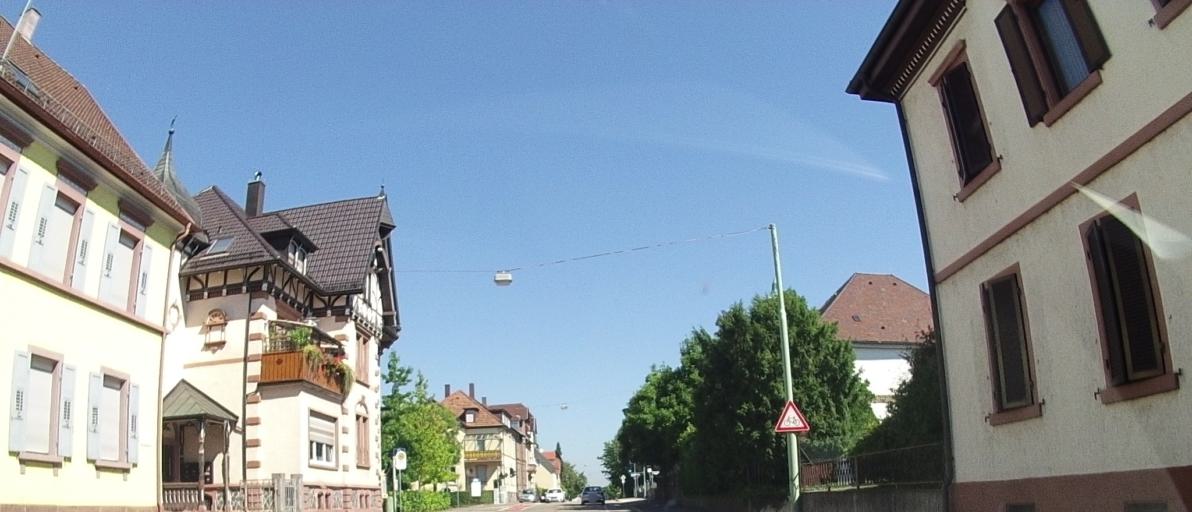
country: DE
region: Baden-Wuerttemberg
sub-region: Karlsruhe Region
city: Buhl
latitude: 48.6985
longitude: 8.1377
